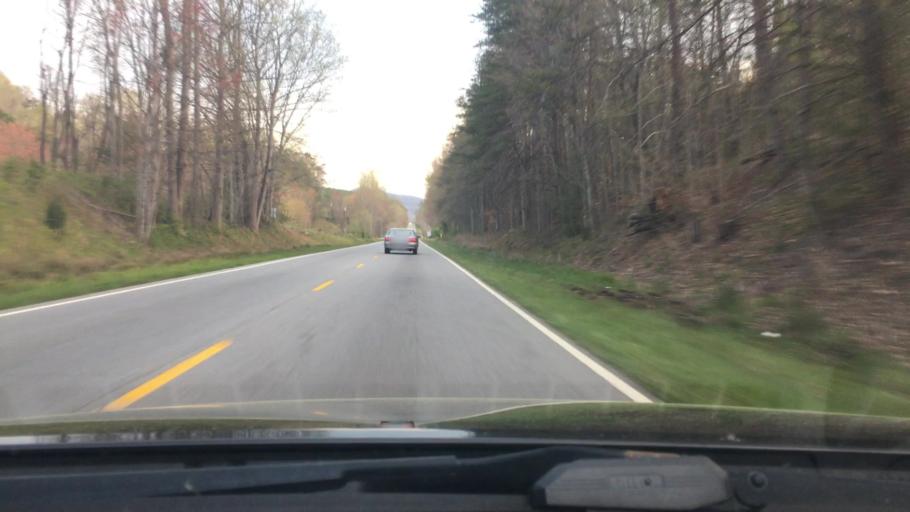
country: US
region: North Carolina
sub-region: McDowell County
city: West Marion
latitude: 35.5914
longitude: -81.9834
